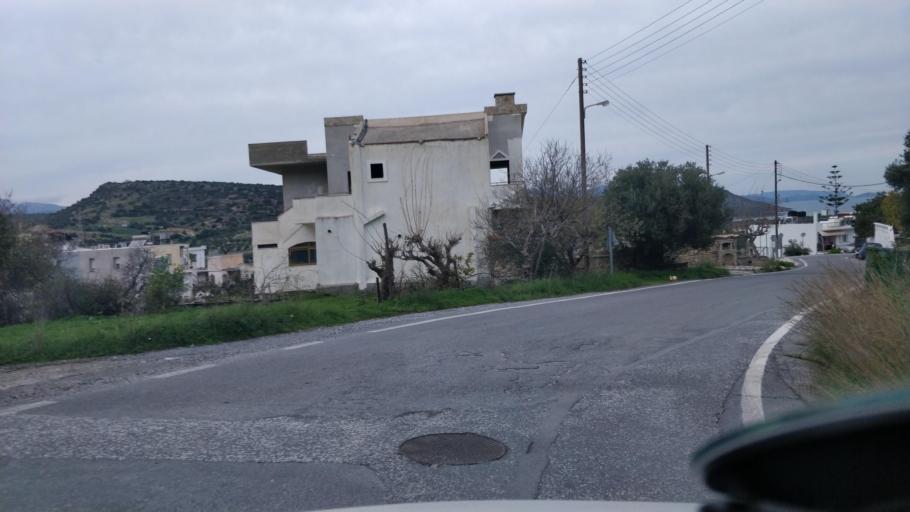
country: GR
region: Crete
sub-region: Nomos Lasithiou
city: Agios Nikolaos
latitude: 35.1157
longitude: 25.7260
